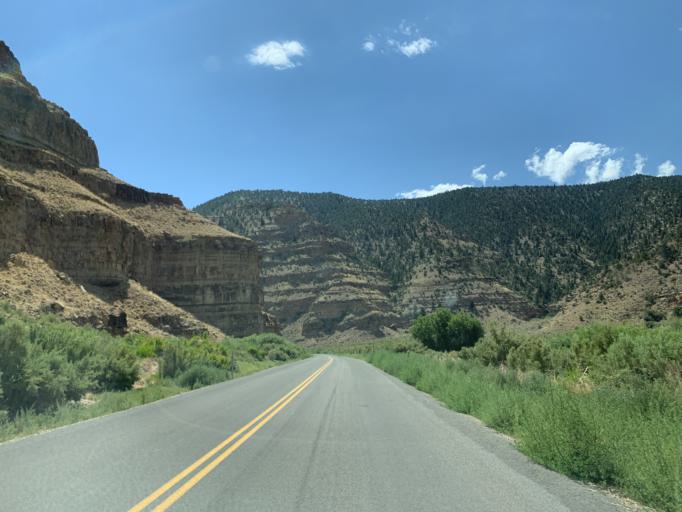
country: US
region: Utah
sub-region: Carbon County
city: East Carbon City
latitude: 39.8099
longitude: -110.2719
